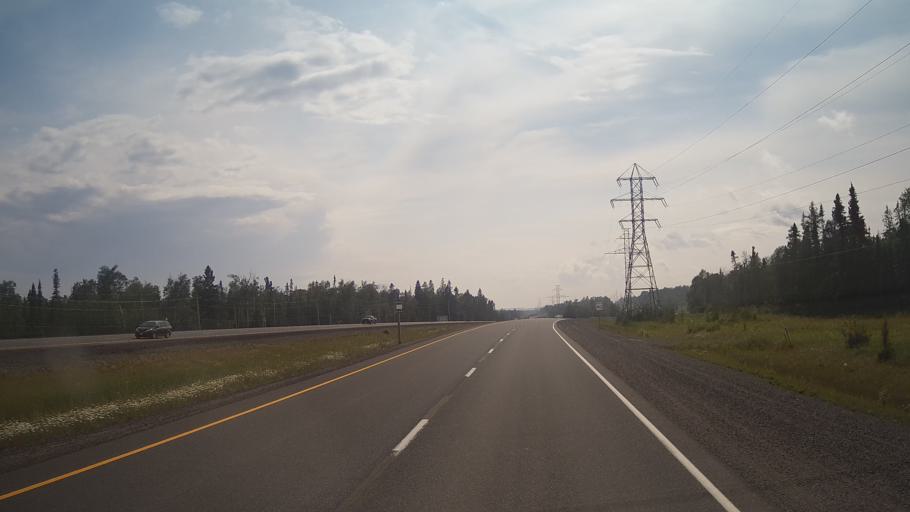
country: CA
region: Ontario
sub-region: Thunder Bay District
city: Thunder Bay
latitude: 48.5702
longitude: -88.8335
